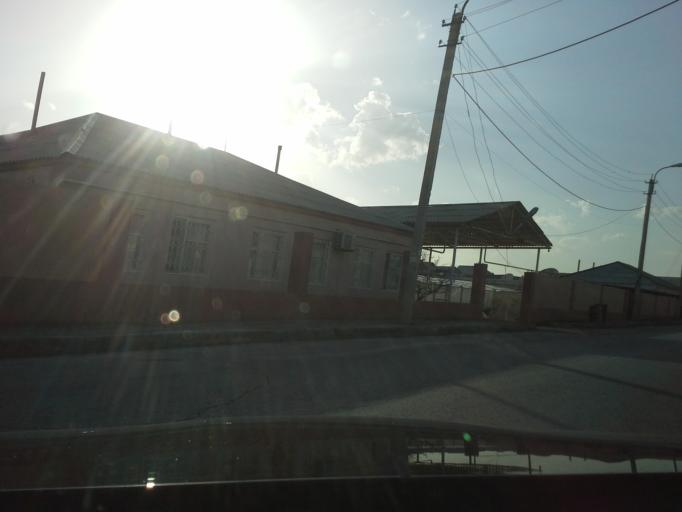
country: TM
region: Ahal
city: Abadan
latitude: 38.0228
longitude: 58.2263
